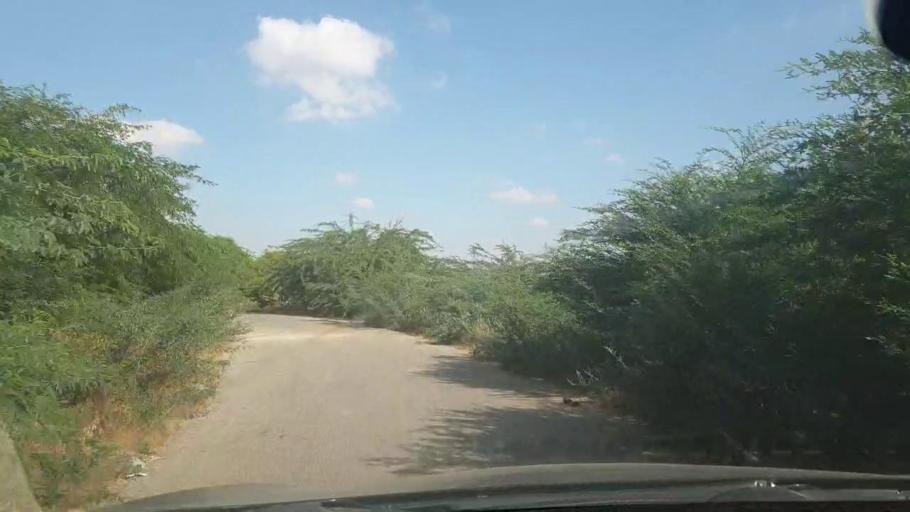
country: PK
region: Sindh
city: Malir Cantonment
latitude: 25.0569
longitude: 67.3910
